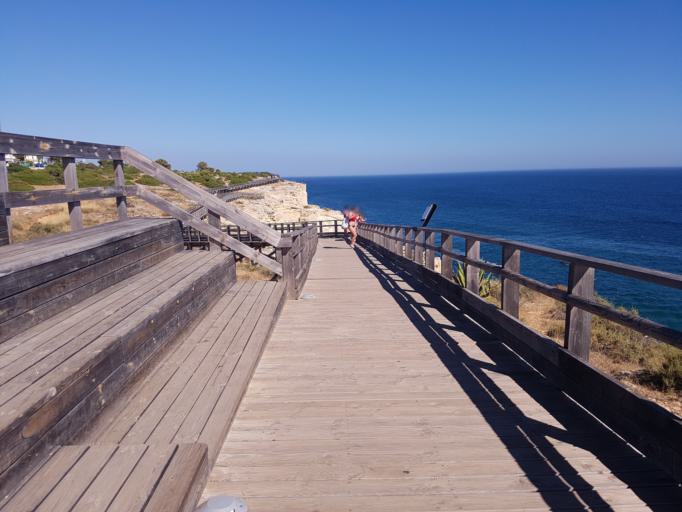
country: PT
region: Faro
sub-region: Lagoa
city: Carvoeiro
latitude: 37.0944
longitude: -8.4696
